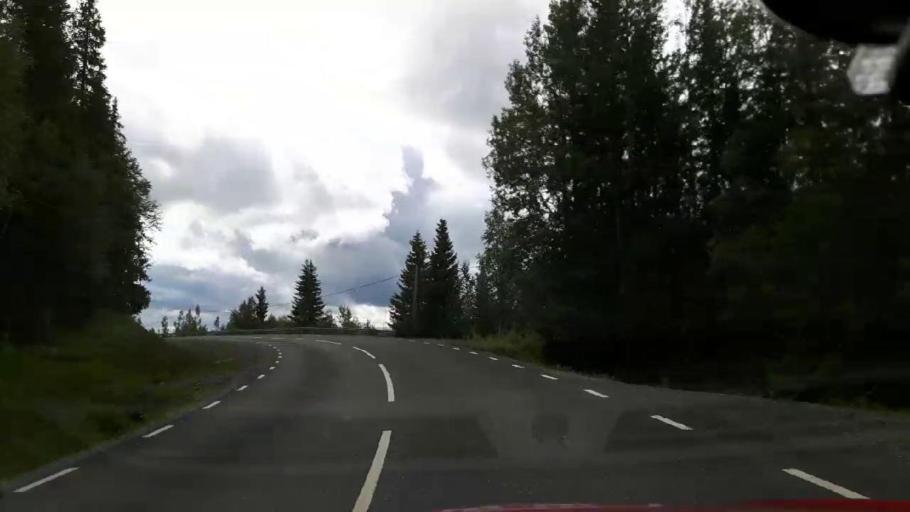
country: NO
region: Nord-Trondelag
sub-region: Lierne
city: Sandvika
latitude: 64.5916
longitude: 14.1148
